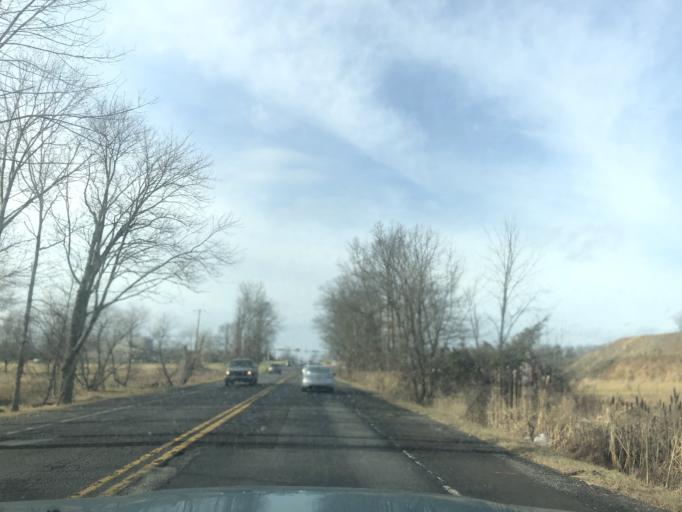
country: US
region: Pennsylvania
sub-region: Bucks County
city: Quakertown
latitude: 40.4424
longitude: -75.3806
